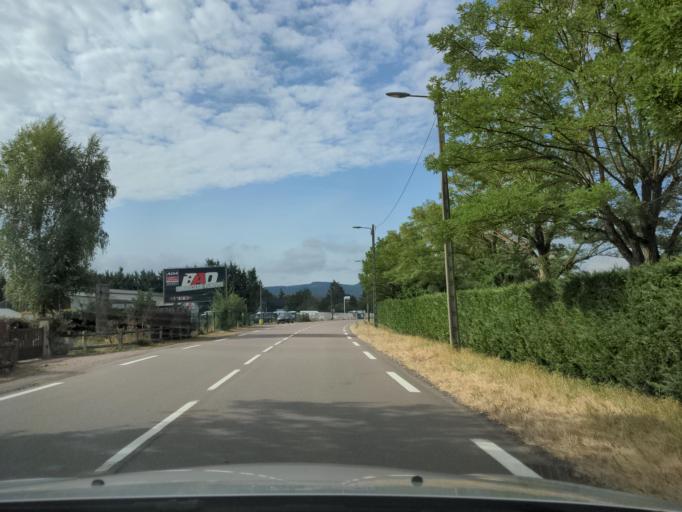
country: FR
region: Bourgogne
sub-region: Departement de Saone-et-Loire
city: Autun
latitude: 46.9773
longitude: 4.3088
